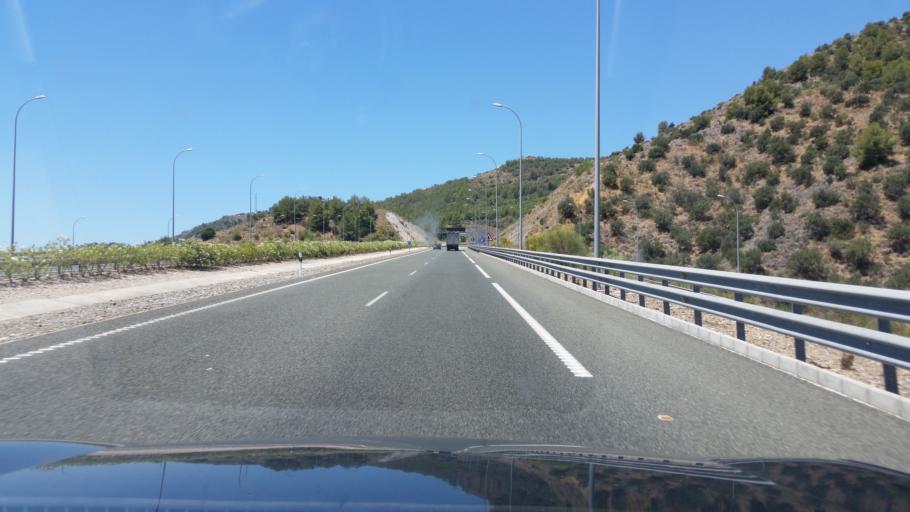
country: ES
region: Andalusia
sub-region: Provincia de Granada
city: La Herradura
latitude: 36.7518
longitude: -3.7523
